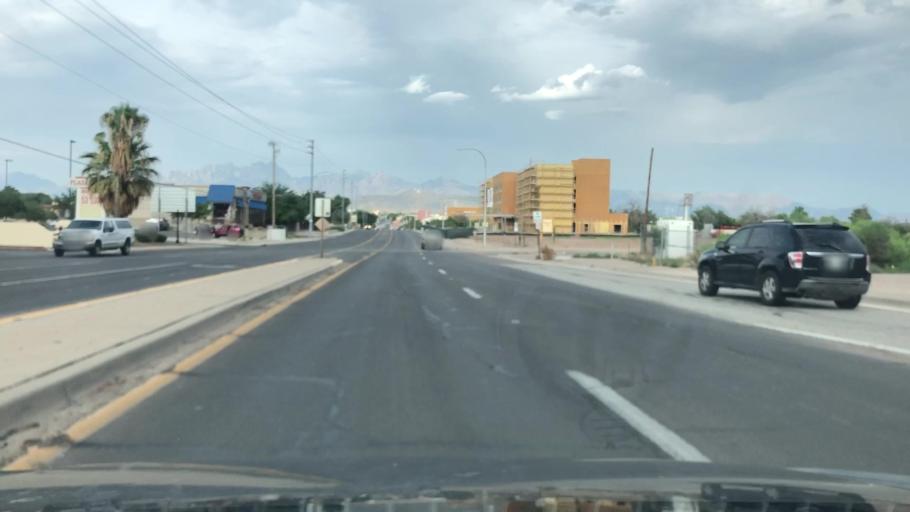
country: US
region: New Mexico
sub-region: Dona Ana County
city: University Park
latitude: 32.2820
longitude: -106.7672
